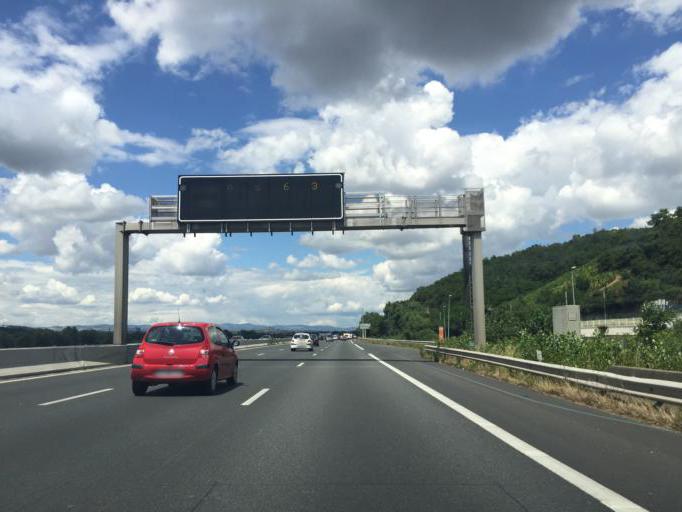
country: FR
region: Rhone-Alpes
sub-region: Departement du Rhone
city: Loire-sur-Rhone
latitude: 45.5599
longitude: 4.8220
